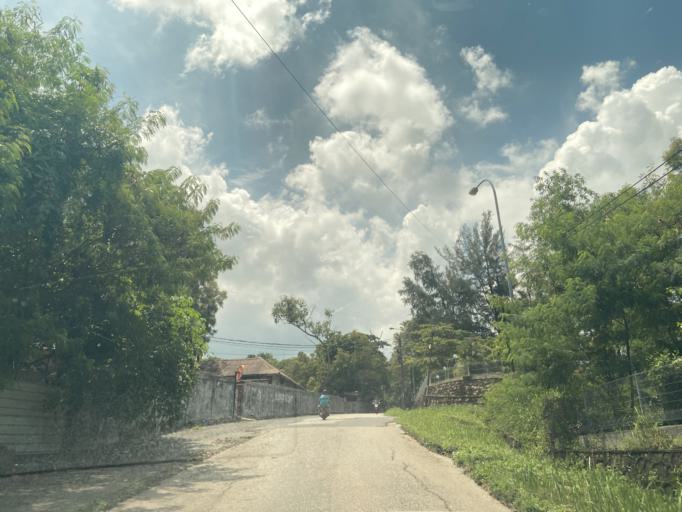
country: SG
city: Singapore
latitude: 1.1529
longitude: 104.0129
